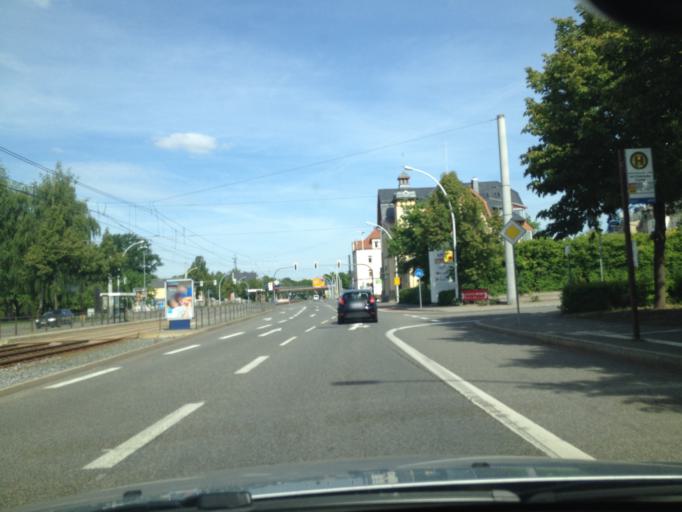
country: DE
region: Saxony
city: Chemnitz
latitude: 50.7960
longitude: 12.9188
